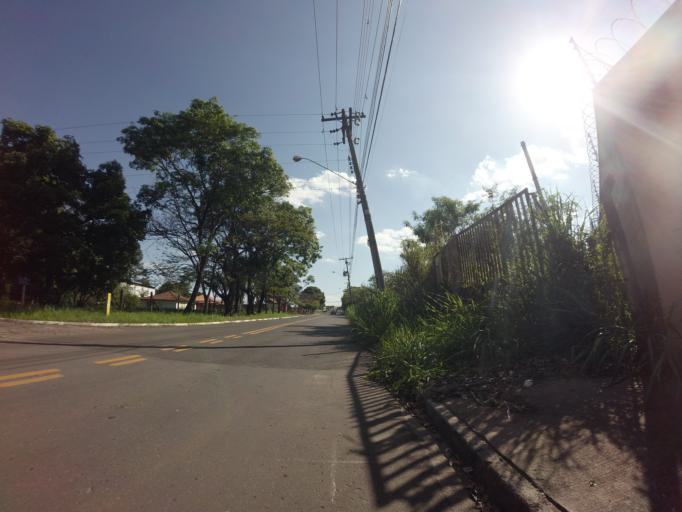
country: BR
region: Sao Paulo
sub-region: Piracicaba
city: Piracicaba
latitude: -22.7428
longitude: -47.5917
